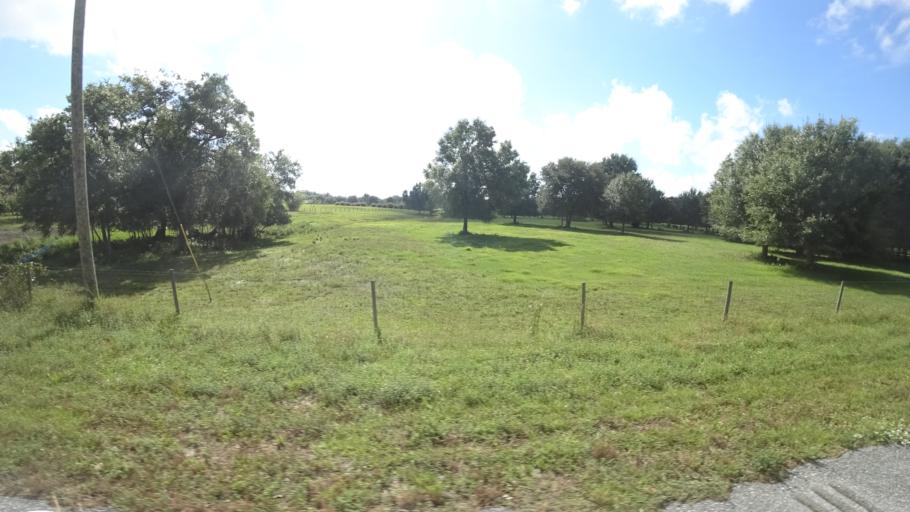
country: US
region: Florida
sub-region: Sarasota County
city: Lake Sarasota
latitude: 27.3510
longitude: -82.2391
